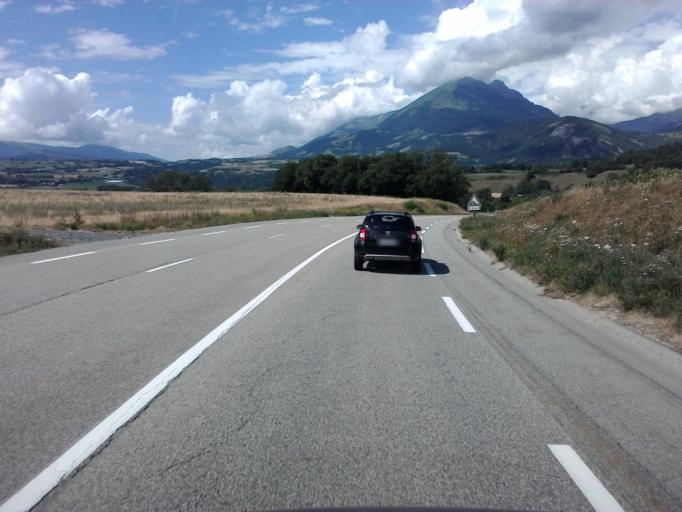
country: FR
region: Rhone-Alpes
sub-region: Departement de l'Isere
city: La Mure
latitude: 44.8841
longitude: 5.8251
